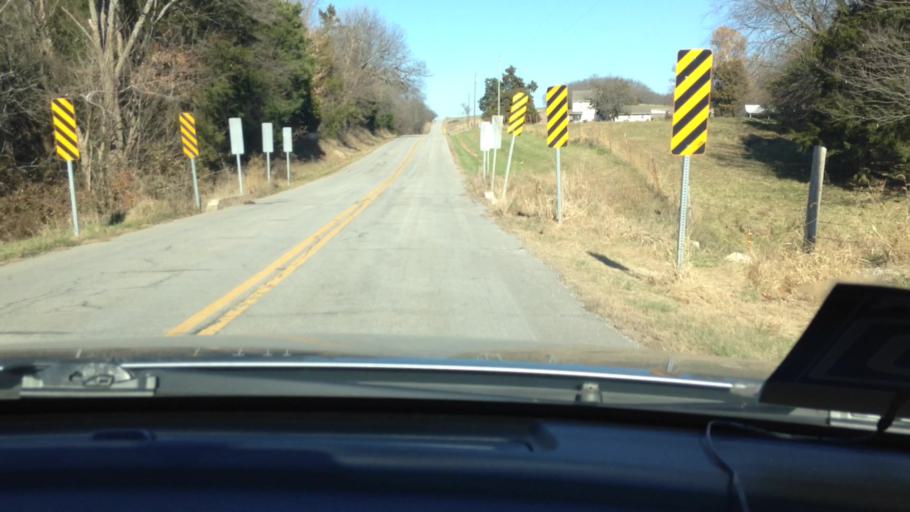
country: US
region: Missouri
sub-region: Platte County
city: Weston
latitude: 39.4686
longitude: -94.9007
